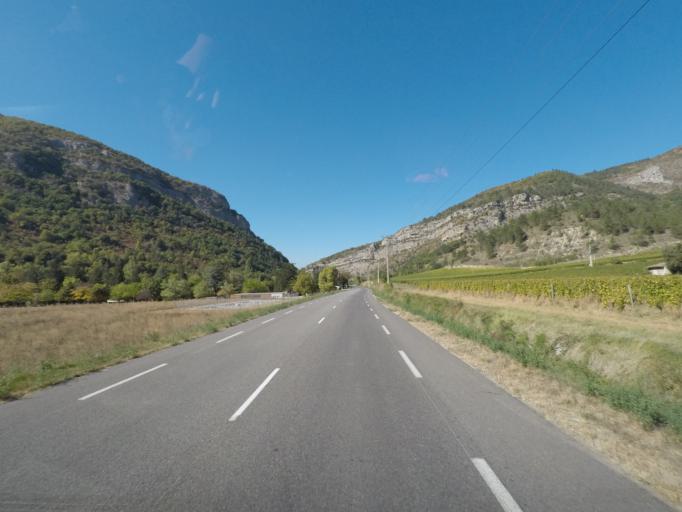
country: FR
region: Rhone-Alpes
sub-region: Departement de la Drome
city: Die
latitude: 44.6895
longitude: 5.2241
